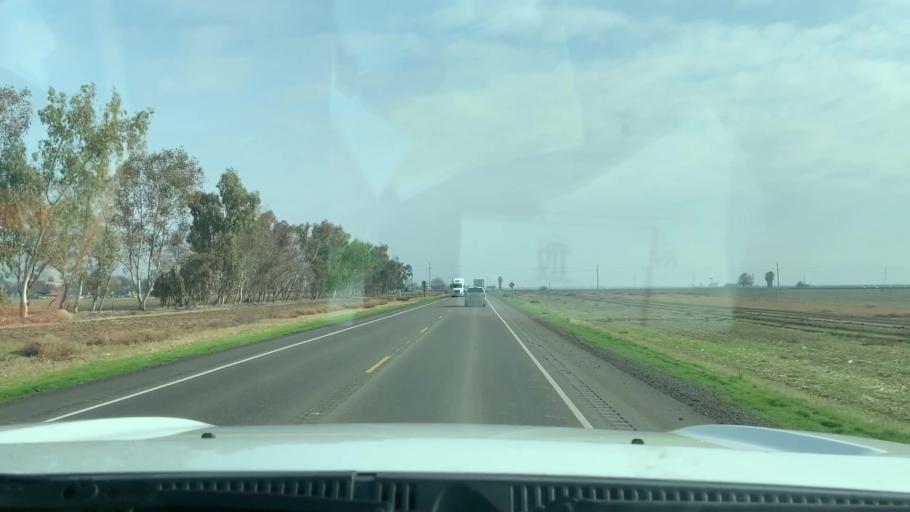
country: US
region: California
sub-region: Kings County
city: Lemoore Station
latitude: 36.2553
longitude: -119.9111
